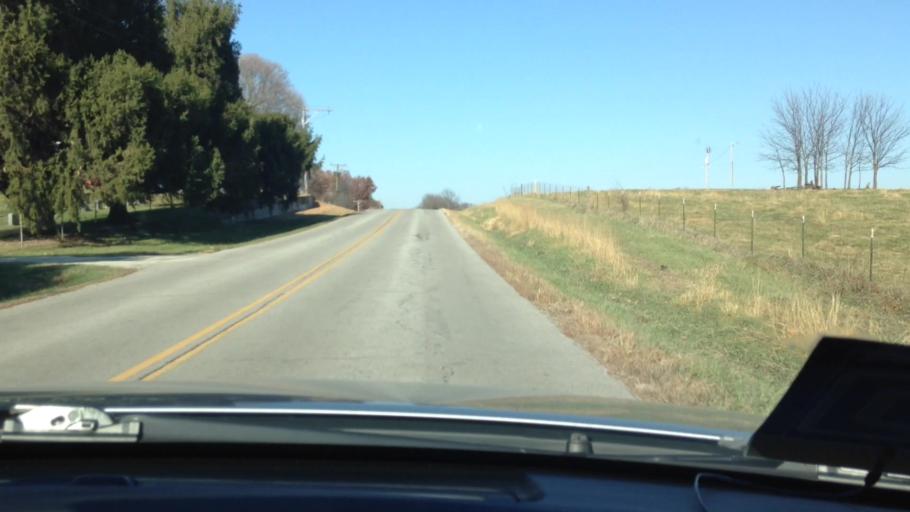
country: US
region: Missouri
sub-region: Platte County
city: Weston
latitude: 39.4313
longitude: -94.8541
